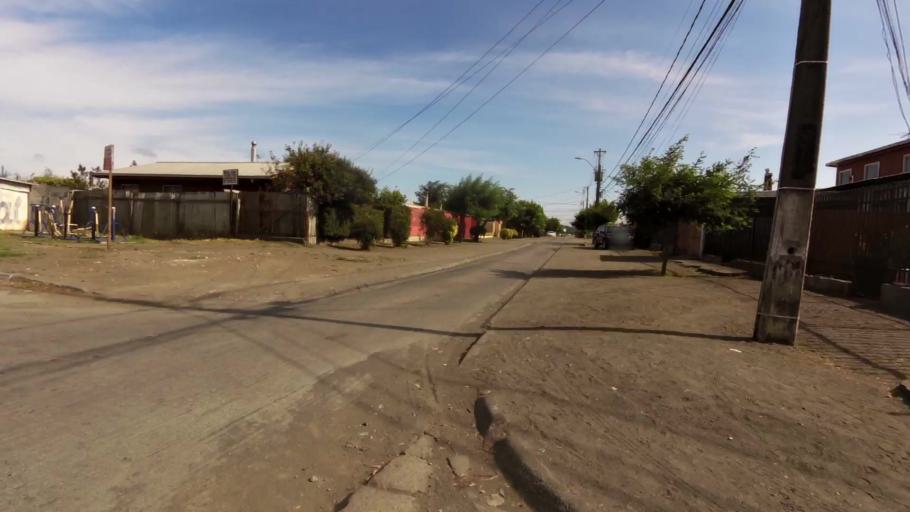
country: CL
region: Biobio
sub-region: Provincia de Concepcion
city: Talcahuano
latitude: -36.7881
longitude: -73.1134
